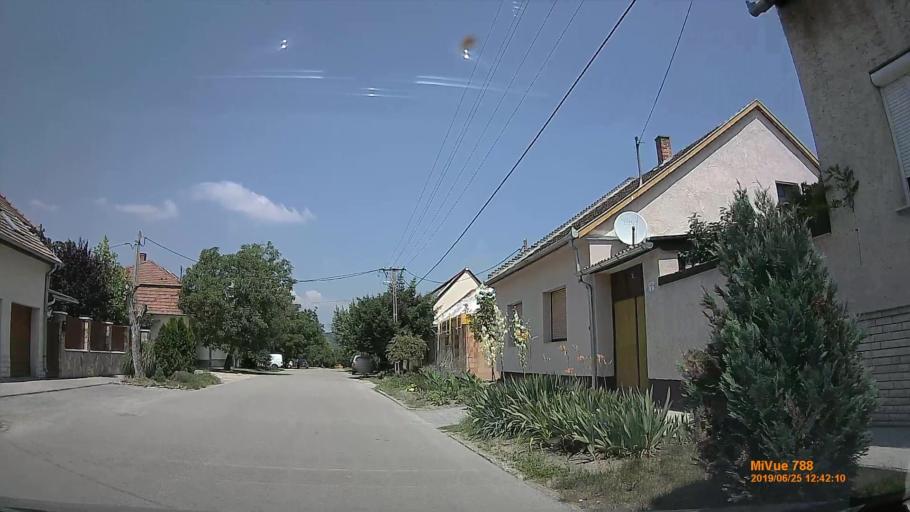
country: HU
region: Komarom-Esztergom
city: Esztergom
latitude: 47.8041
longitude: 18.7413
